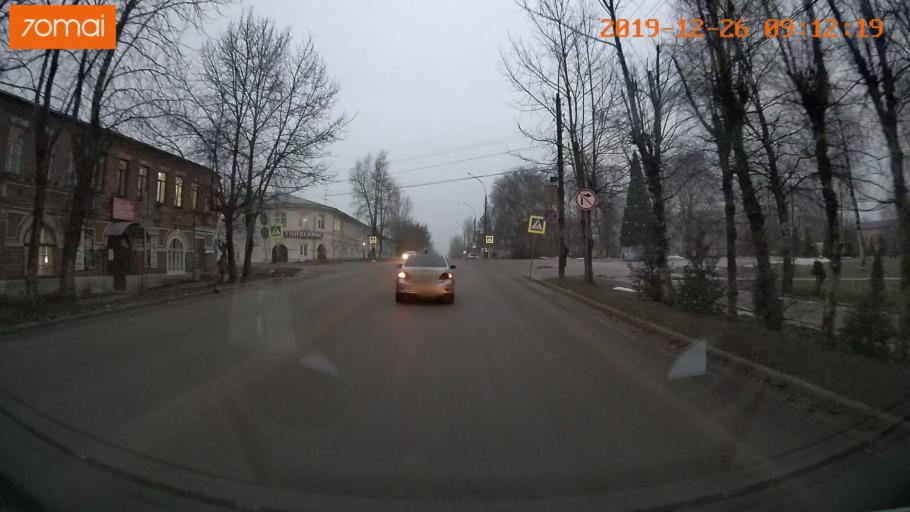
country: RU
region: Vologda
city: Gryazovets
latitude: 58.8803
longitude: 40.2533
